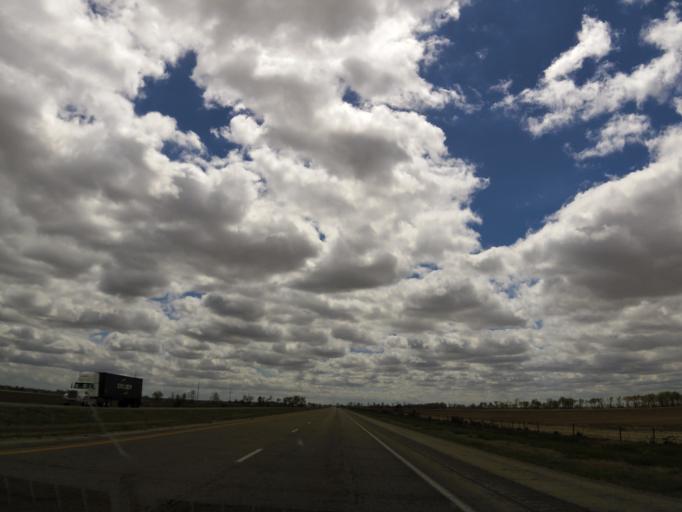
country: US
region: Arkansas
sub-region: Poinsett County
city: Trumann
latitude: 35.5940
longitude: -90.4968
